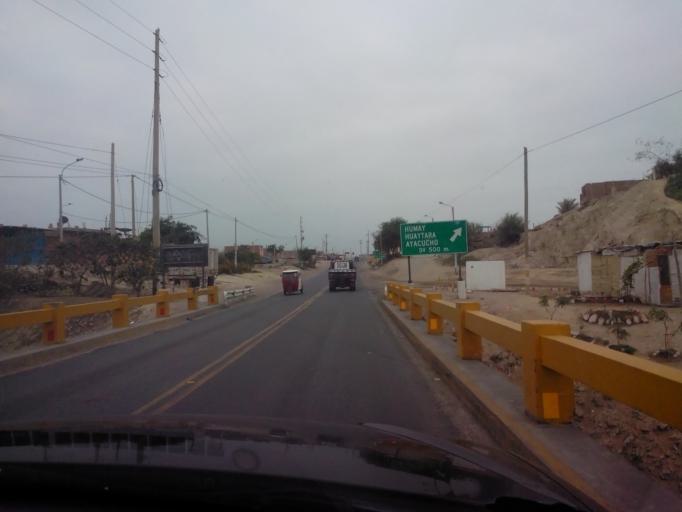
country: PE
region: Ica
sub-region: Provincia de Pisco
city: San Clemente
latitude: -13.6871
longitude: -76.1584
